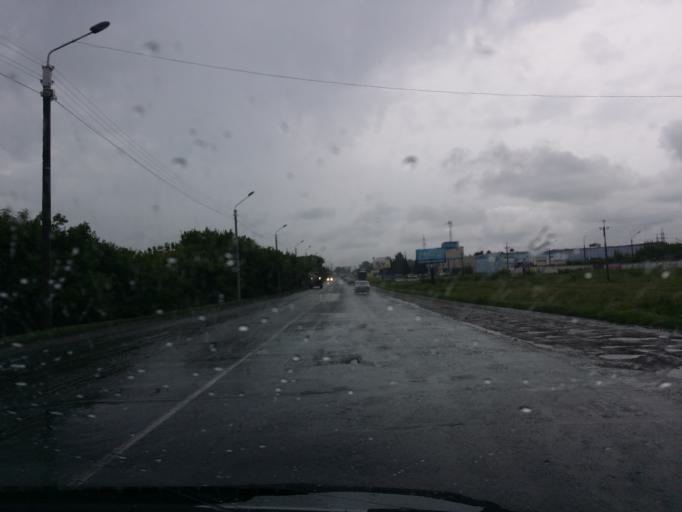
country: RU
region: Altai Krai
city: Novosilikatnyy
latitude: 53.3499
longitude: 83.6107
